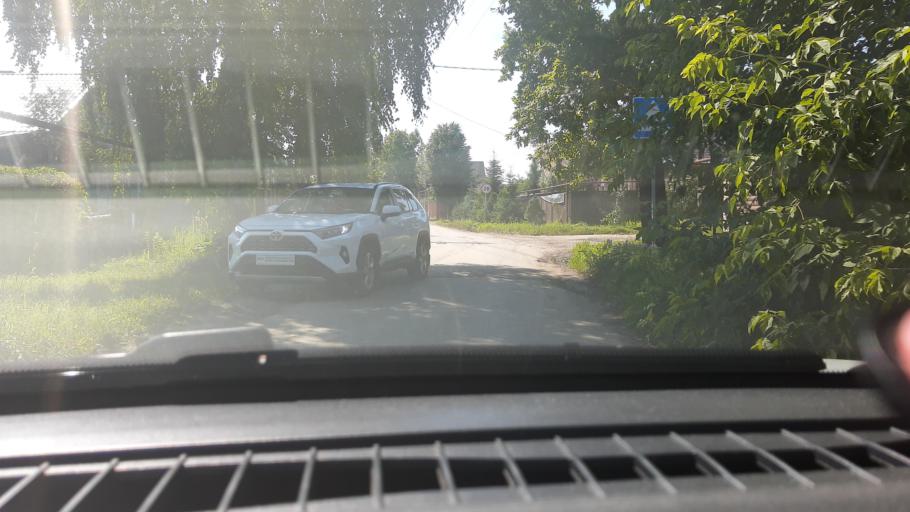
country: RU
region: Nizjnij Novgorod
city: Afonino
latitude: 56.2714
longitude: 44.1959
